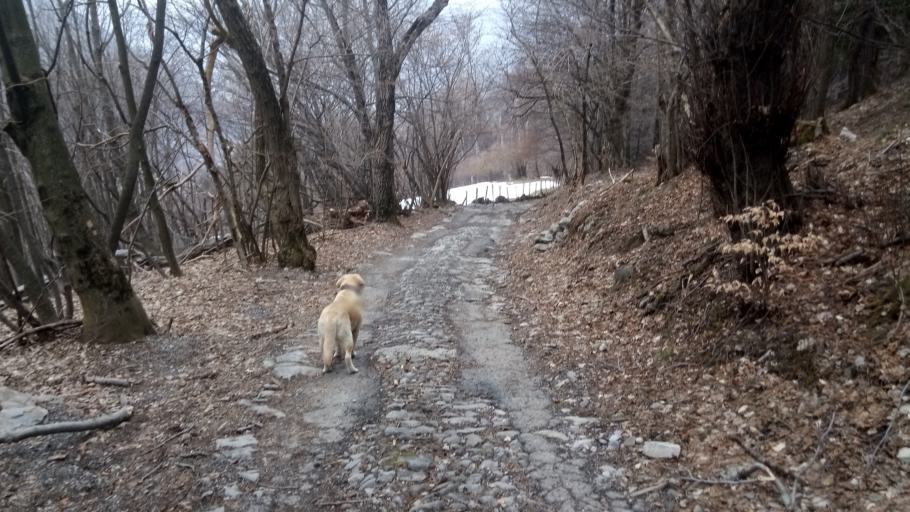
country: IT
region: Lombardy
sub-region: Provincia di Como
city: Occagno
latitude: 45.9116
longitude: 9.1000
